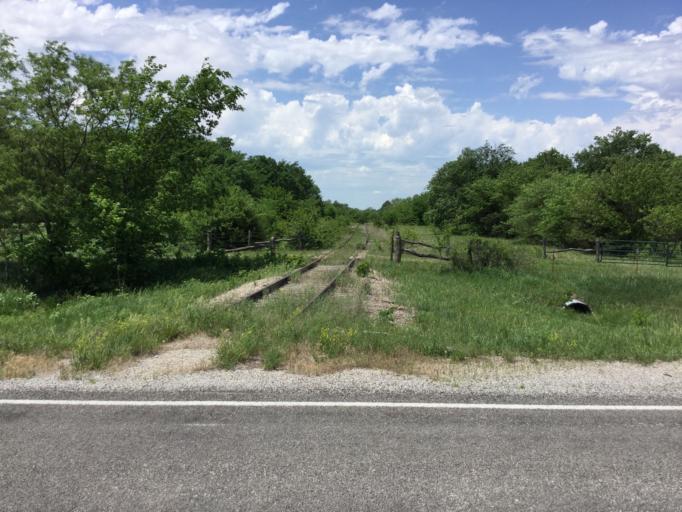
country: US
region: Kansas
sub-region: Coffey County
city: Burlington
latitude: 38.1759
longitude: -95.5544
